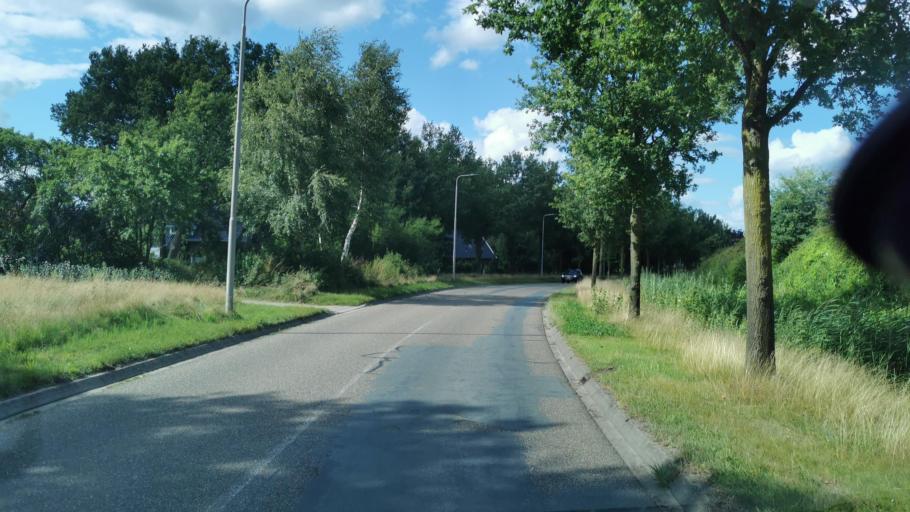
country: NL
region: Overijssel
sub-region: Gemeente Losser
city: Losser
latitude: 52.2648
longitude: 6.9919
